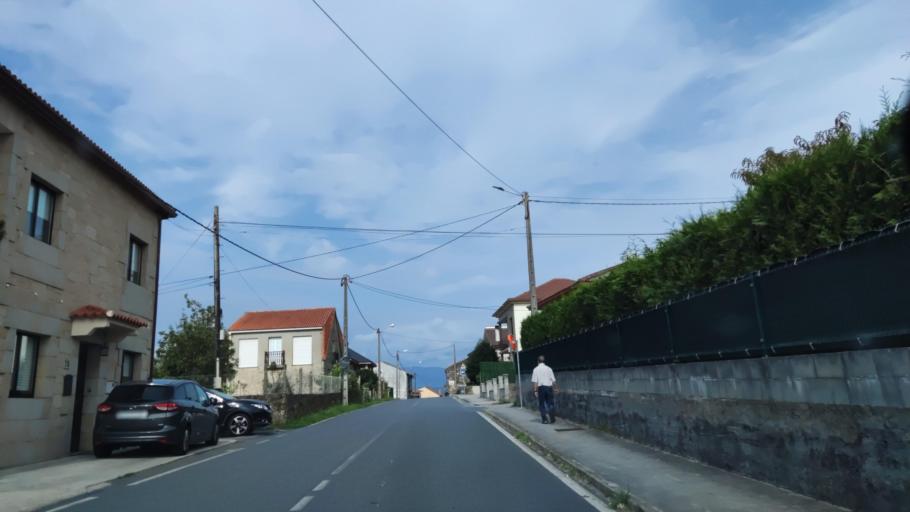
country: ES
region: Galicia
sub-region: Provincia da Coruna
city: Rianxo
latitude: 42.6473
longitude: -8.8090
